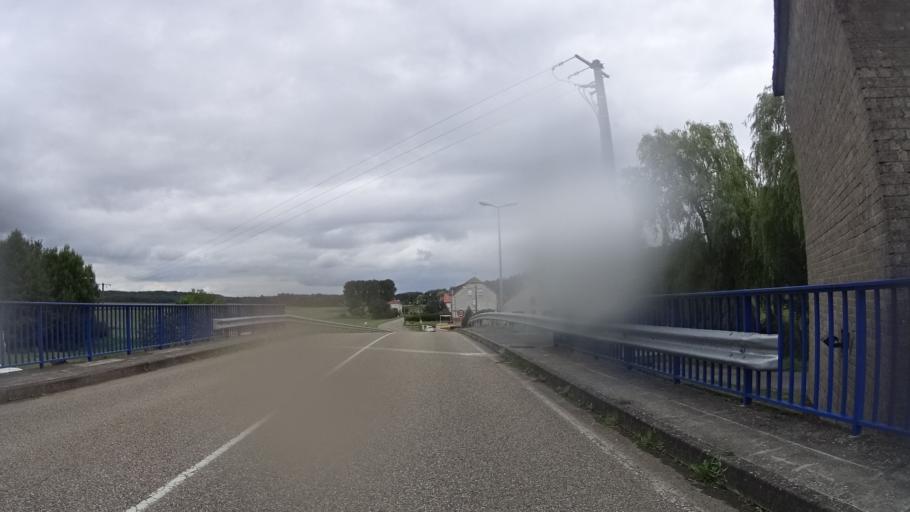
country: FR
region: Lorraine
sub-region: Departement de la Moselle
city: Dieuze
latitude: 48.6787
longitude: 6.7893
